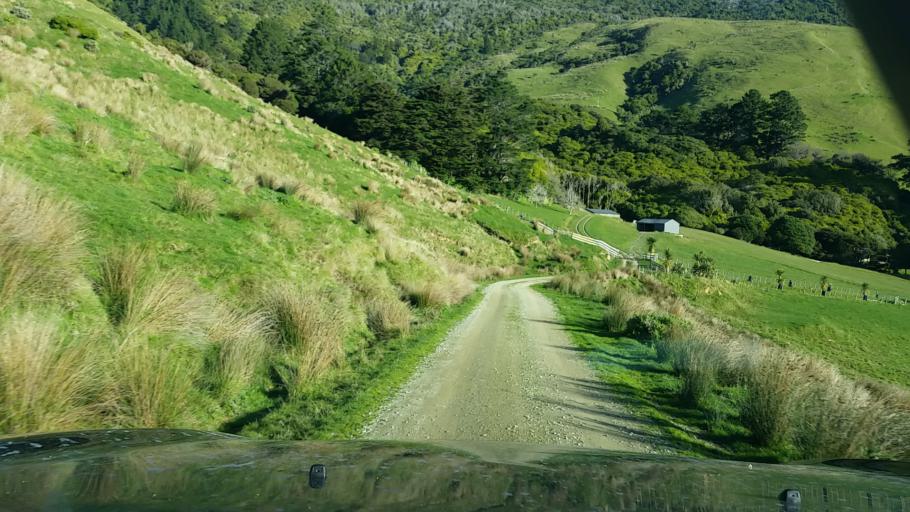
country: NZ
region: Marlborough
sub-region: Marlborough District
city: Picton
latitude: -41.0204
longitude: 174.1385
